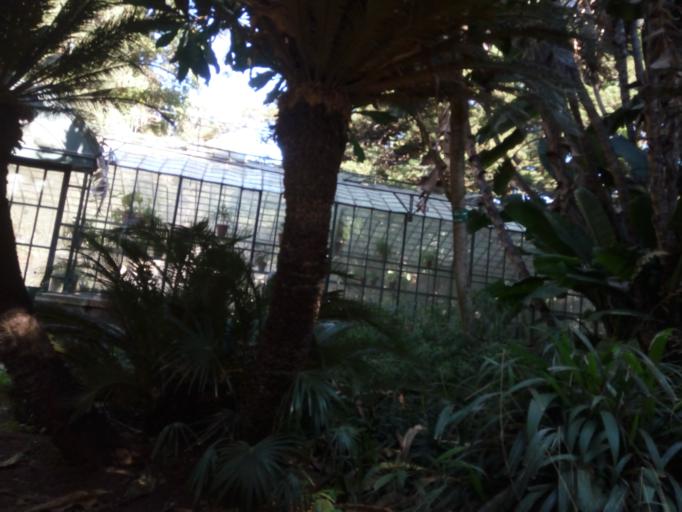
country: DZ
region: Alger
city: Algiers
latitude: 36.7464
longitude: 3.0747
